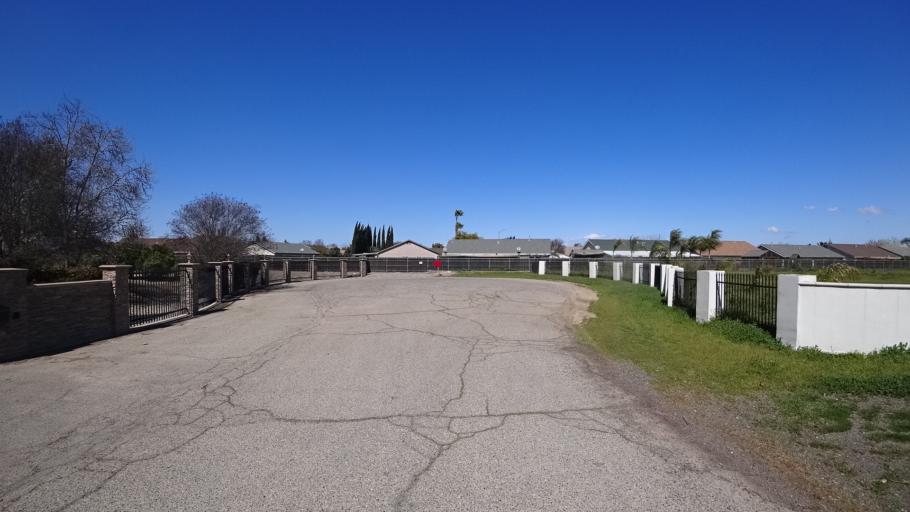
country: US
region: California
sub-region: Fresno County
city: West Park
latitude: 36.7678
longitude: -119.8657
